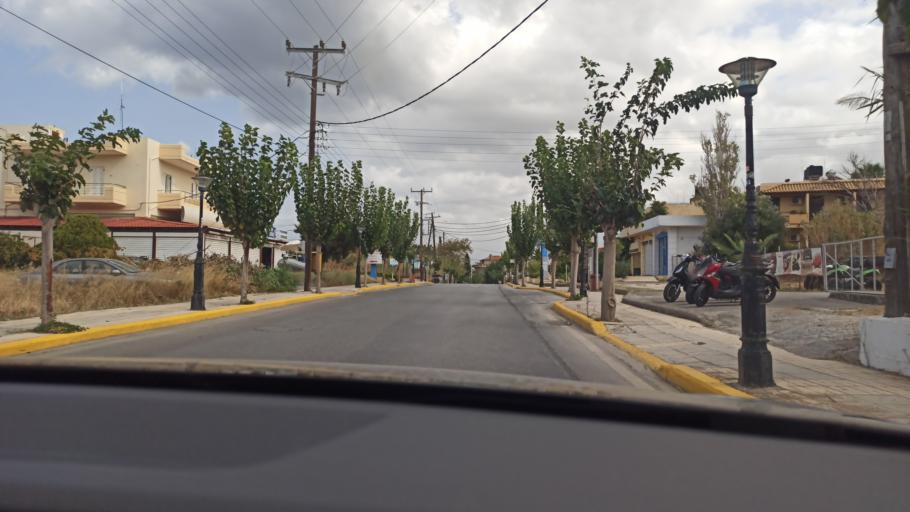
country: GR
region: Crete
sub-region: Nomos Irakleiou
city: Gazi
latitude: 35.3352
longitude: 25.0622
